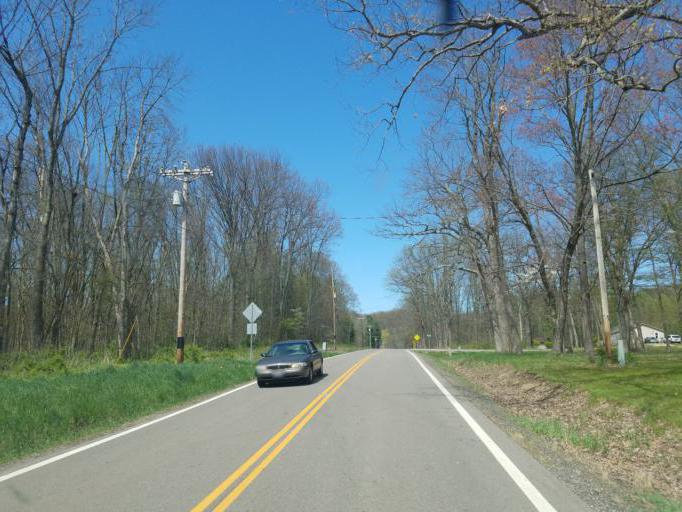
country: US
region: Ohio
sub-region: Ashland County
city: Ashland
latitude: 40.7553
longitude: -82.3588
